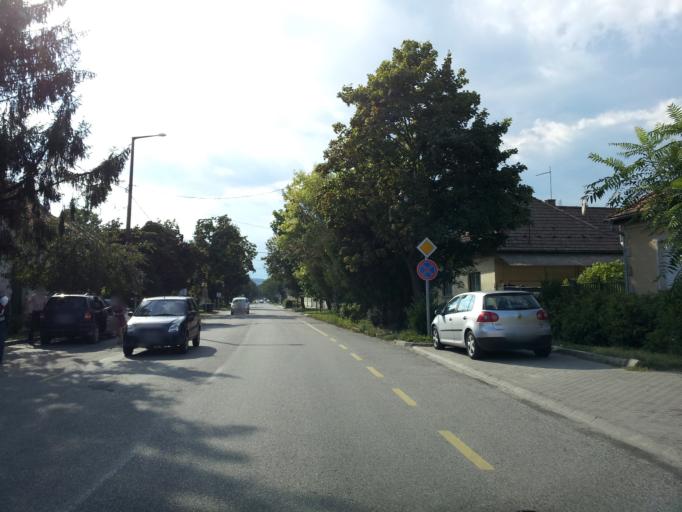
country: HU
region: Pest
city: Veroce
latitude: 47.8224
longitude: 19.0339
